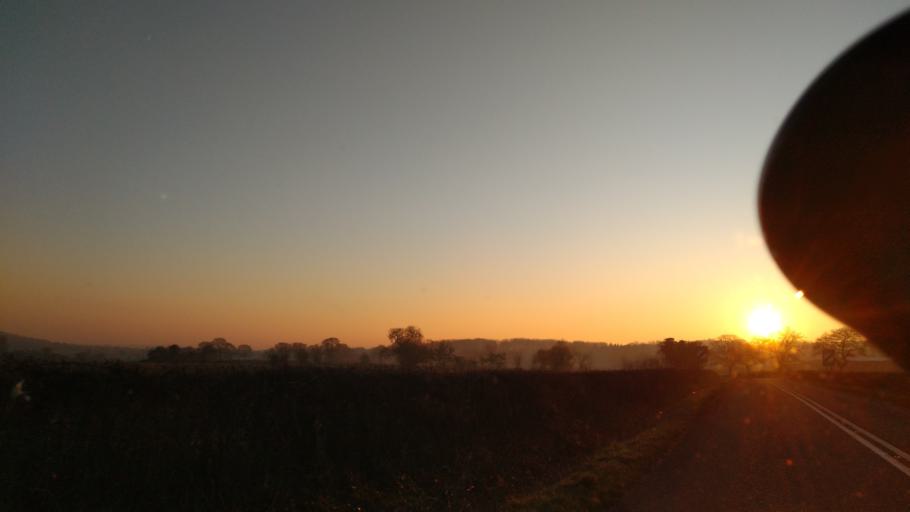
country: GB
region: England
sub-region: Wiltshire
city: Calne
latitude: 51.4171
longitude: -2.0179
